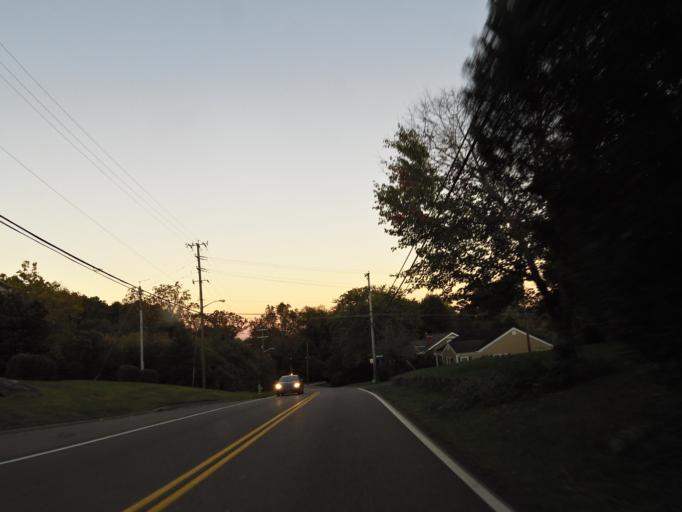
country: US
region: Tennessee
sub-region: Knox County
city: Knoxville
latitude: 36.0306
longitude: -83.9437
